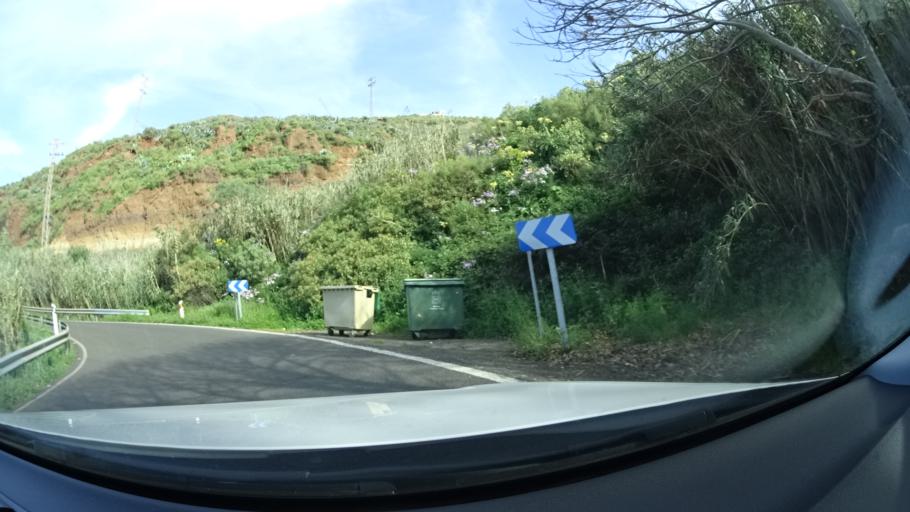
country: ES
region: Canary Islands
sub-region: Provincia de Las Palmas
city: Guia
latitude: 28.1079
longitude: -15.6408
